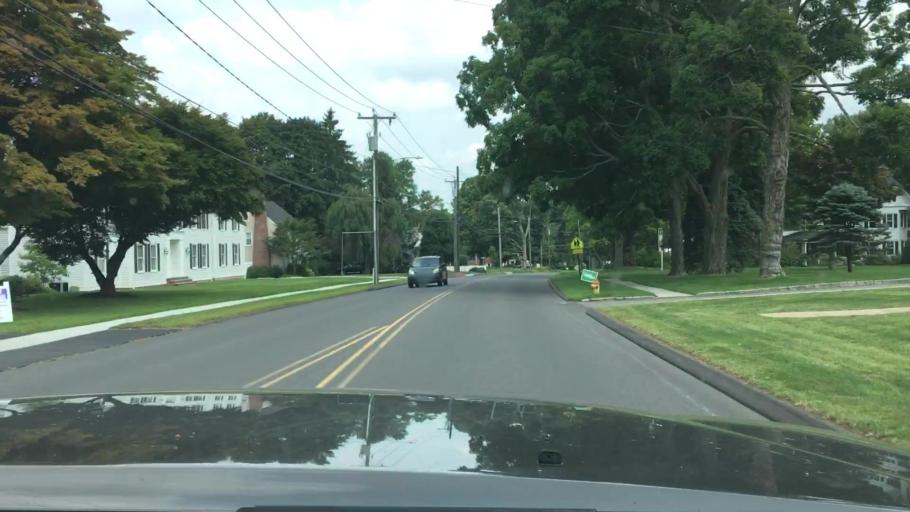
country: US
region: Connecticut
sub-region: New Haven County
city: Cheshire Village
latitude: 41.5096
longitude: -72.9024
